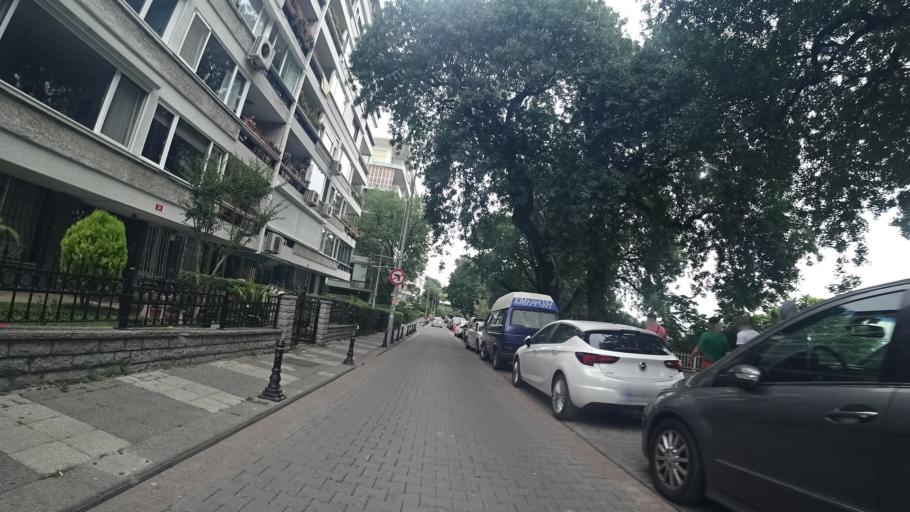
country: TR
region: Istanbul
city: UEskuedar
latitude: 40.9791
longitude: 29.0229
